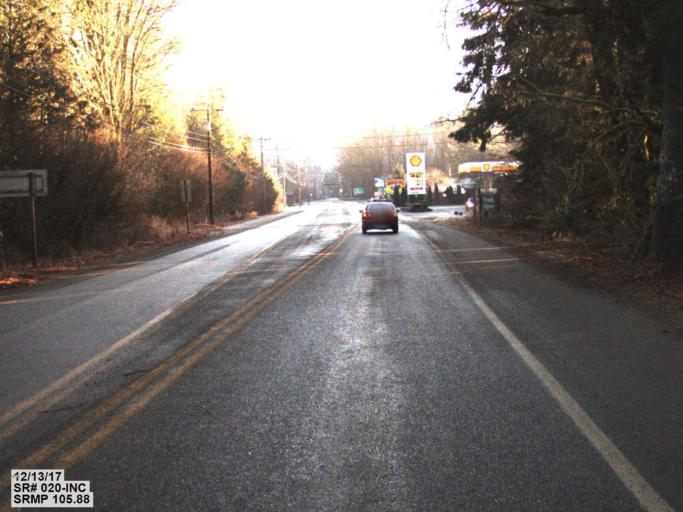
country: US
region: Washington
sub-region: Snohomish County
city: Darrington
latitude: 48.5267
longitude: -121.4362
